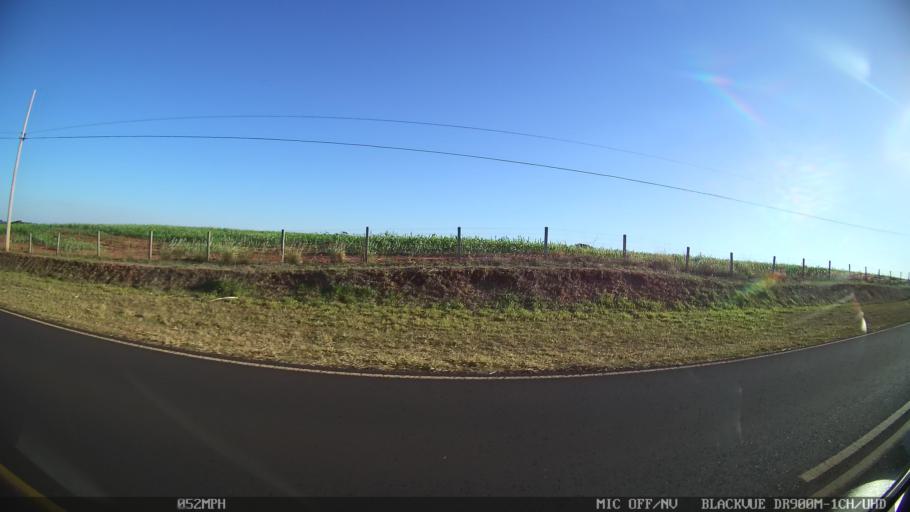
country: BR
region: Sao Paulo
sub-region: Guapiacu
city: Guapiacu
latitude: -20.7846
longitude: -49.2568
